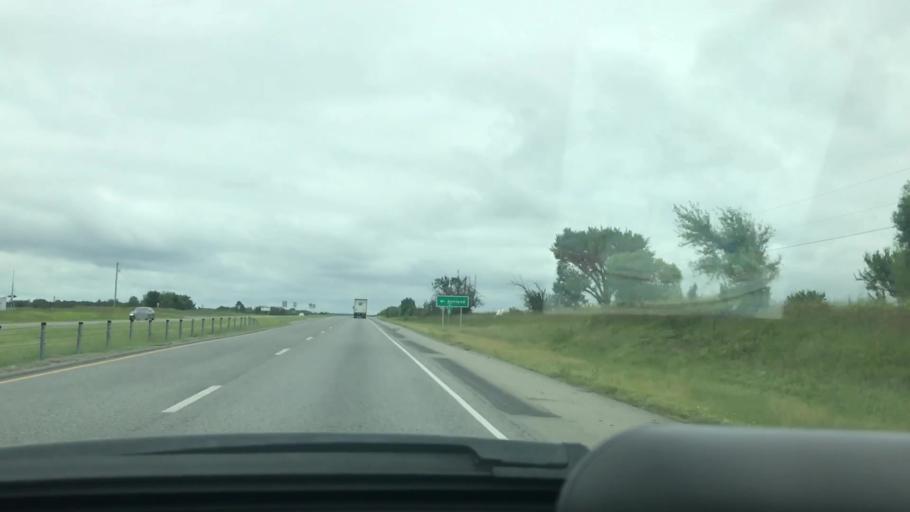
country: US
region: Oklahoma
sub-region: Pittsburg County
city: McAlester
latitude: 34.7515
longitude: -95.8938
